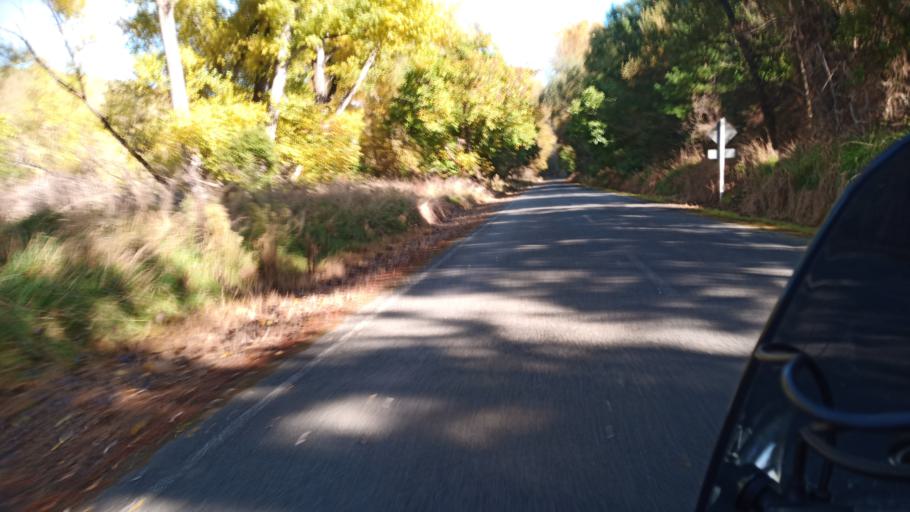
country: NZ
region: Hawke's Bay
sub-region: Wairoa District
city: Wairoa
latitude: -38.9202
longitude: 177.2528
